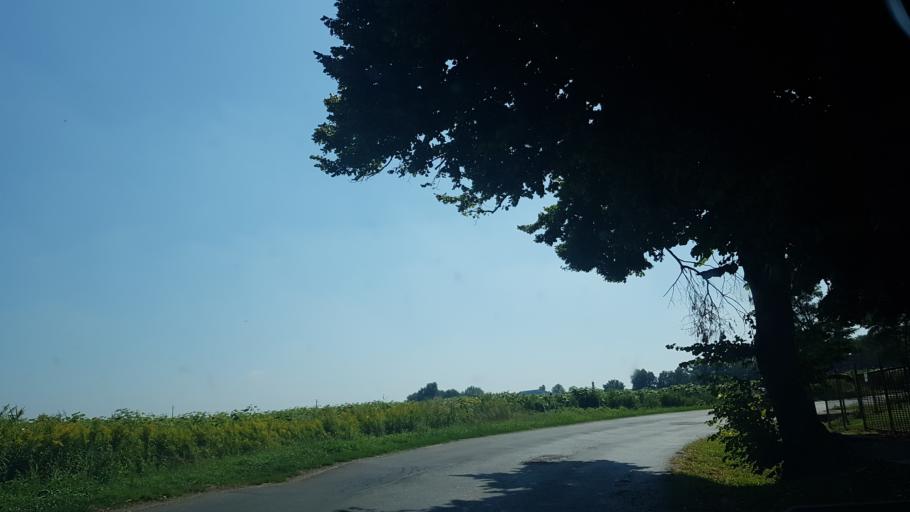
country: HU
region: Somogy
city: Segesd
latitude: 46.3280
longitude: 17.3380
